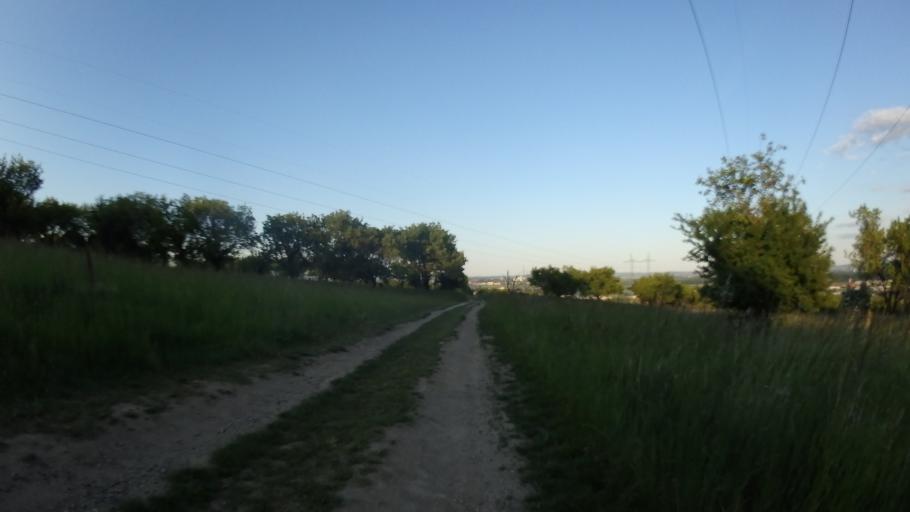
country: CZ
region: South Moravian
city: Zelesice
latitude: 49.1248
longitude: 16.5905
